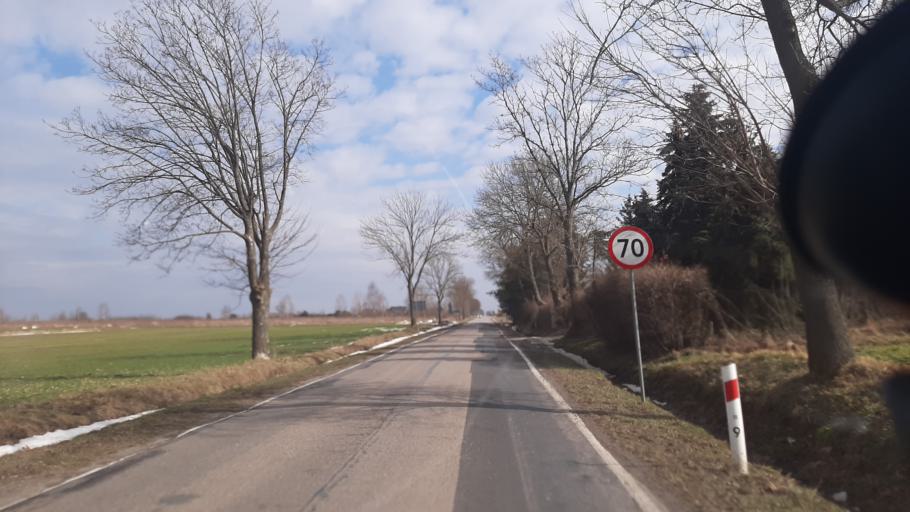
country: PL
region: Lublin Voivodeship
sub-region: Powiat lubelski
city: Niemce
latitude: 51.3611
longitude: 22.5637
